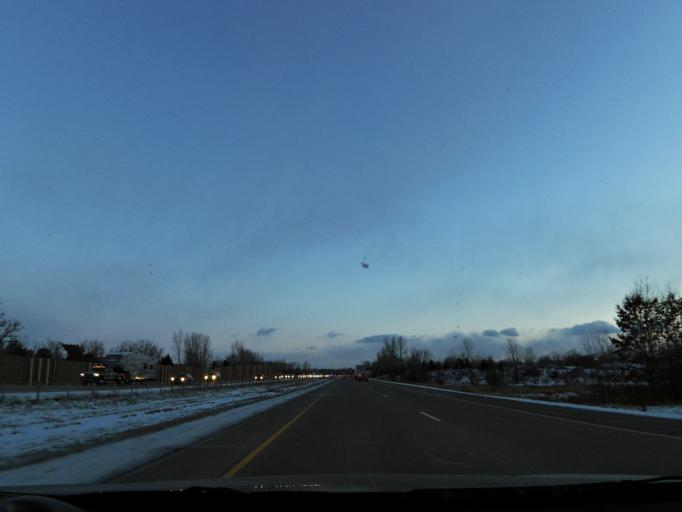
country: US
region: Minnesota
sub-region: Ramsey County
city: North Saint Paul
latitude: 45.0144
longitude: -92.9588
